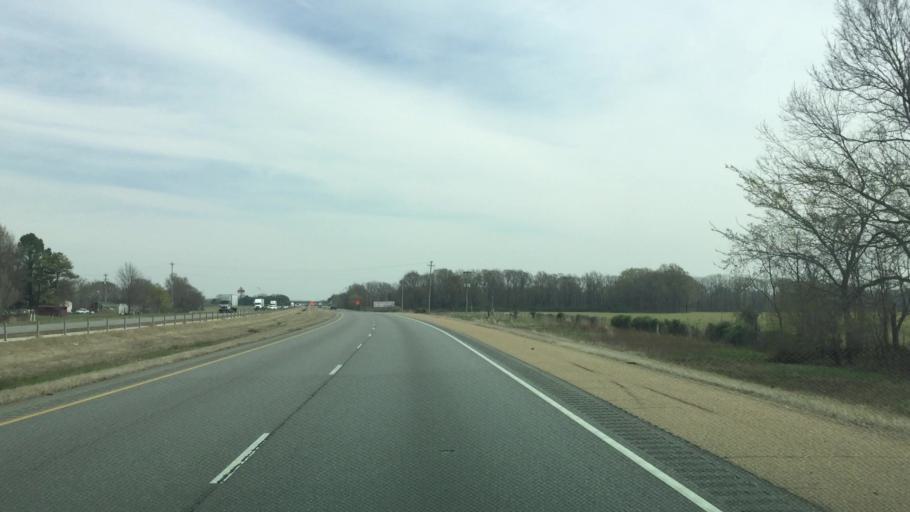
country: US
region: Arkansas
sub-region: Saint Francis County
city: Forrest City
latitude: 34.9776
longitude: -90.9195
